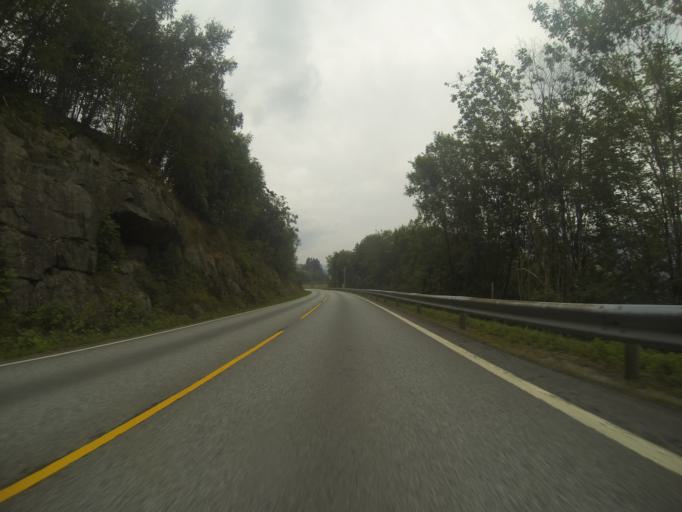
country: NO
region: Rogaland
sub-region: Suldal
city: Sand
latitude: 59.5606
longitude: 6.2685
